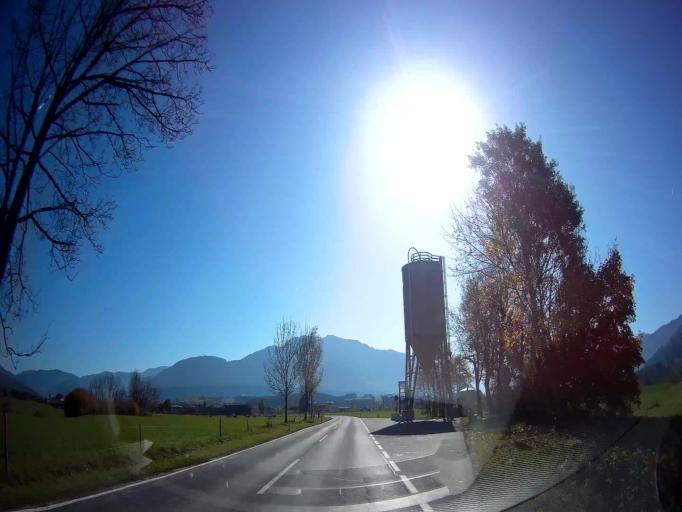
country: AT
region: Salzburg
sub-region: Politischer Bezirk Zell am See
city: Saalfelden am Steinernen Meer
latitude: 47.4345
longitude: 12.8266
